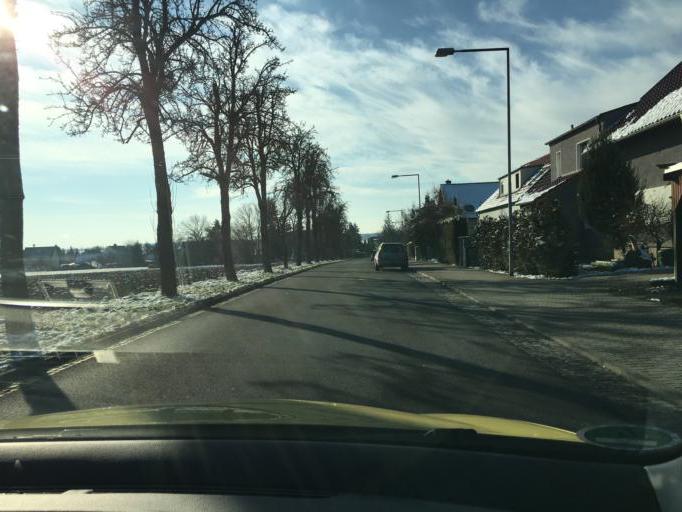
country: DE
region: Saxony
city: Belgershain
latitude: 51.2595
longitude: 12.5327
